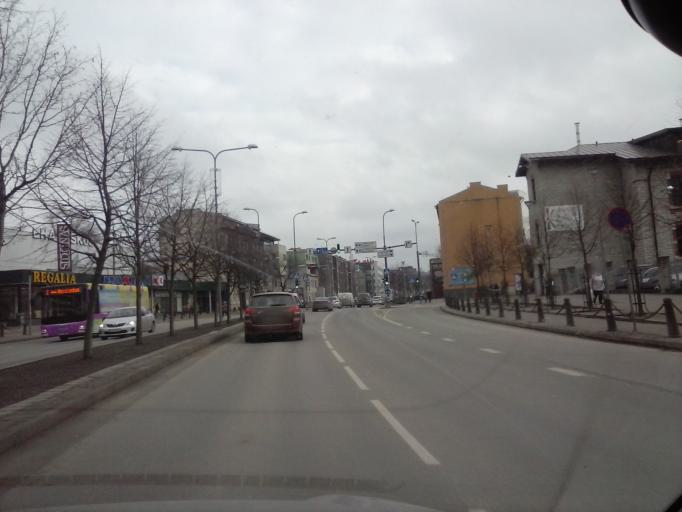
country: EE
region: Harju
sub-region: Tallinna linn
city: Tallinn
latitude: 59.4317
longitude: 24.7679
